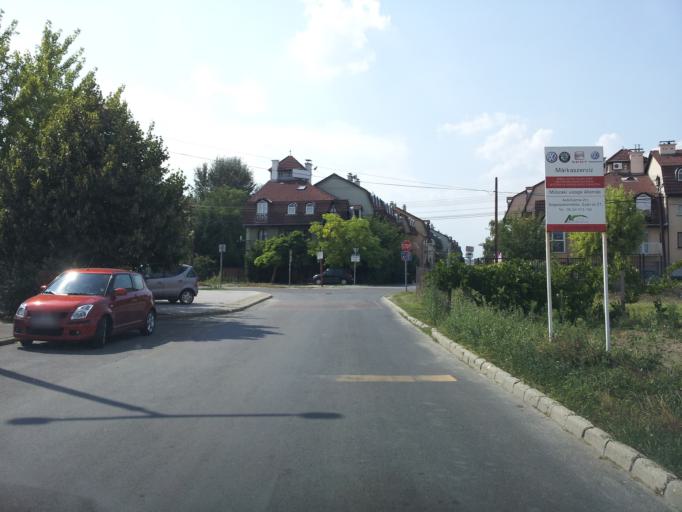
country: HU
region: Pest
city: Szigetszentmiklos
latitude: 47.3427
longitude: 19.0332
